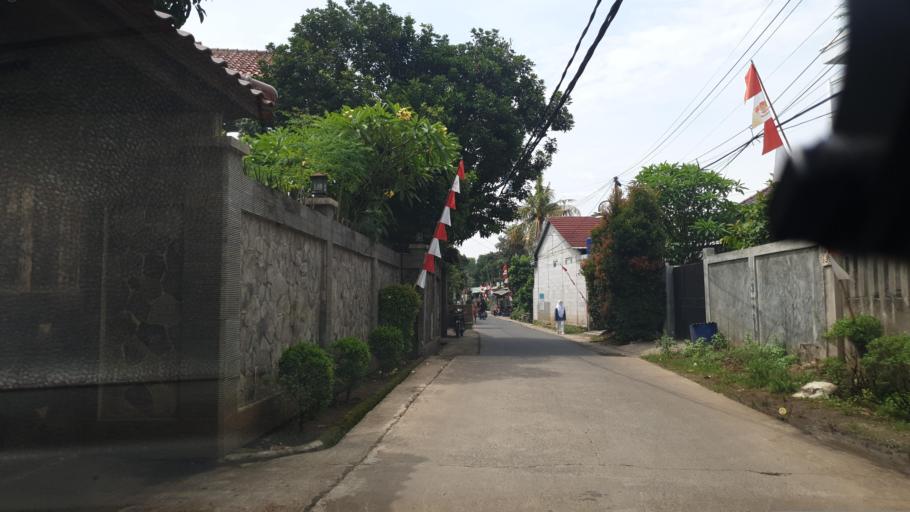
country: ID
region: West Java
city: Sawangan
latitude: -6.3700
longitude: 106.7630
